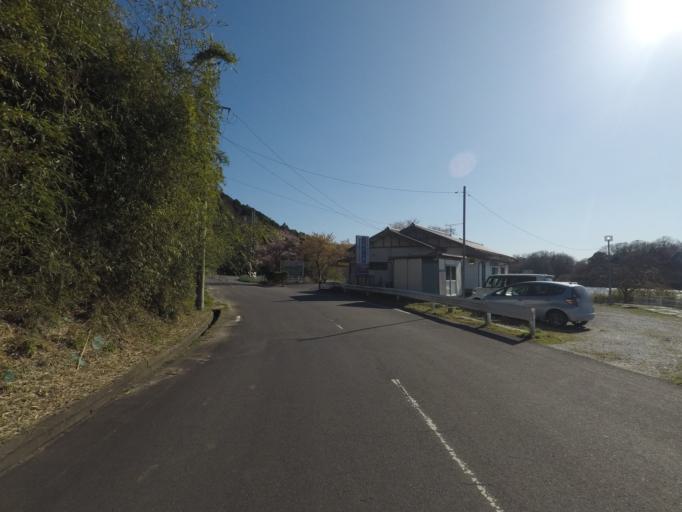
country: JP
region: Ibaraki
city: Makabe
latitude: 36.2399
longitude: 140.0726
